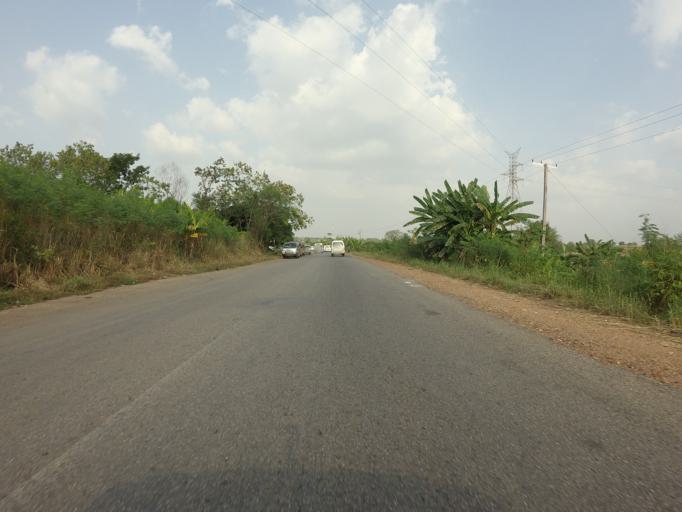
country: GH
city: Akropong
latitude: 6.2417
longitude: 0.1136
